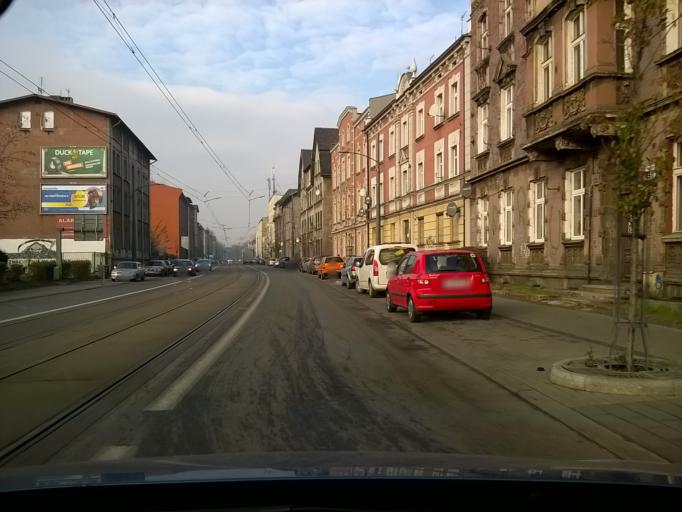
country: PL
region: Silesian Voivodeship
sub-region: Swietochlowice
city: Swietochlowice
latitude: 50.2802
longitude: 18.9425
